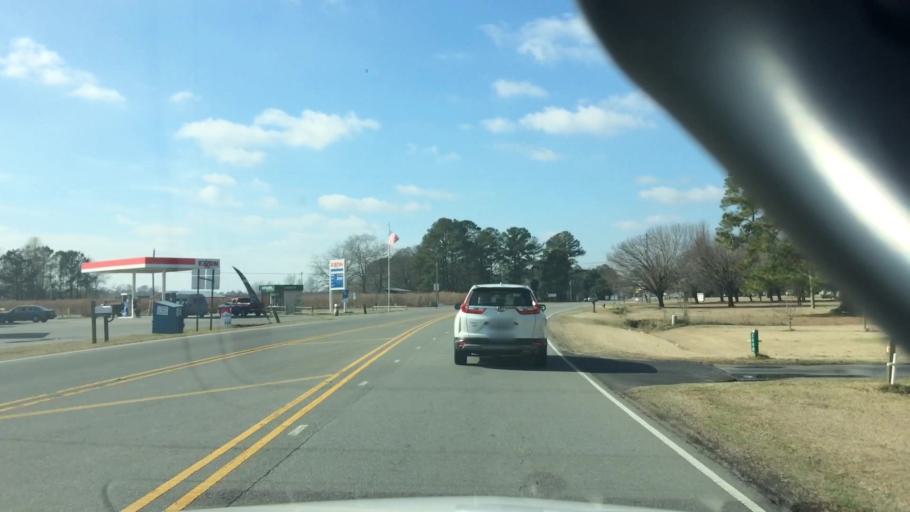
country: US
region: North Carolina
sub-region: Duplin County
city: Beulaville
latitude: 34.8295
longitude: -77.8111
